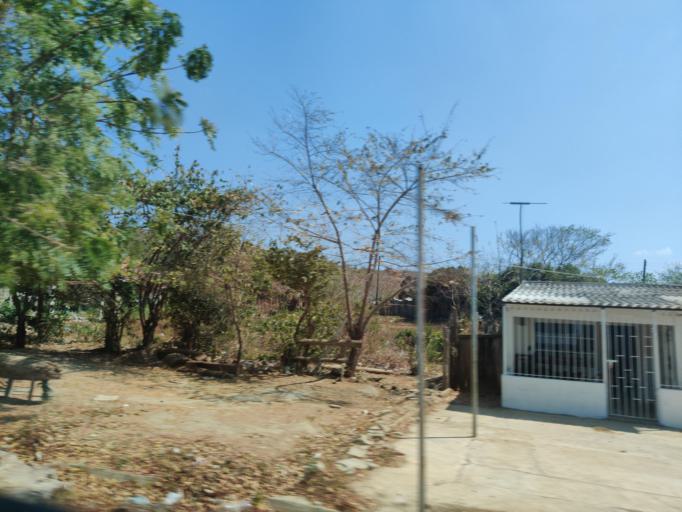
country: CO
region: Bolivar
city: Santa Catalina
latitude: 10.7417
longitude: -75.2626
